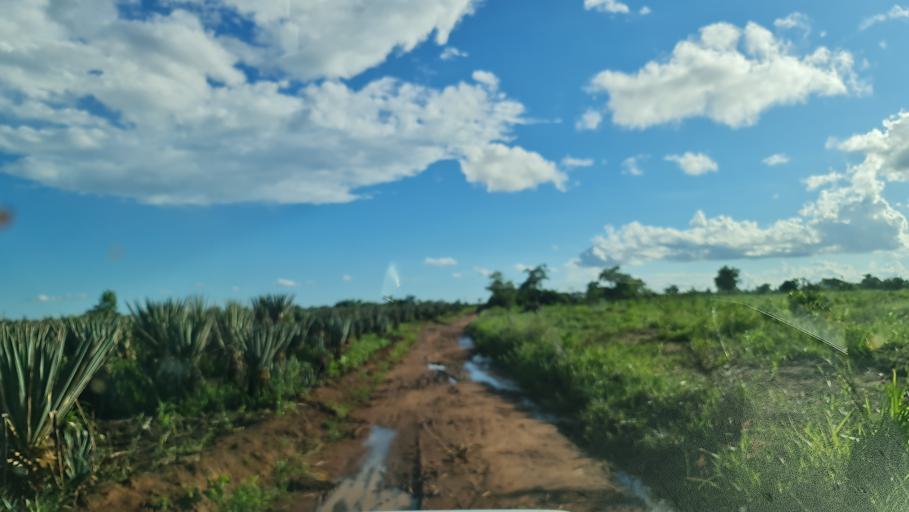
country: MZ
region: Nampula
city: Ilha de Mocambique
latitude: -14.9398
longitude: 40.2003
